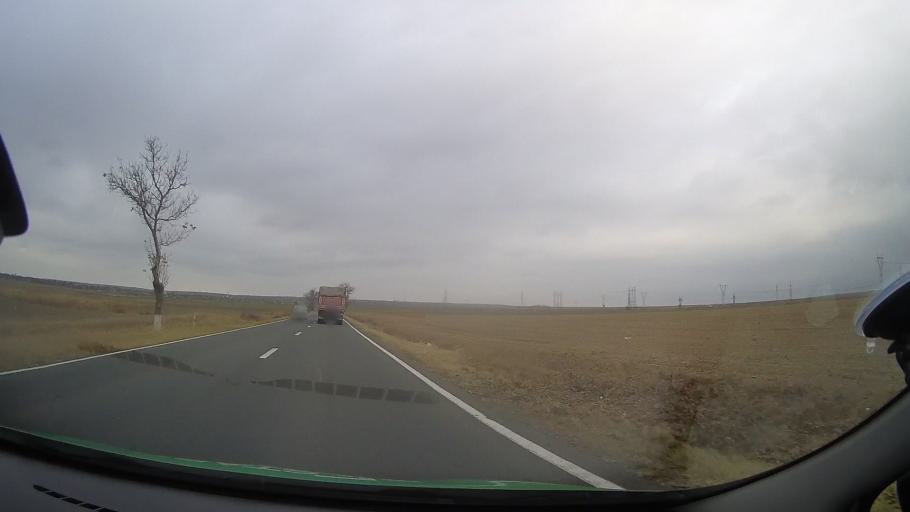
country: RO
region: Constanta
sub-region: Comuna Castelu
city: Castelu
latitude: 44.2516
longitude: 28.3554
